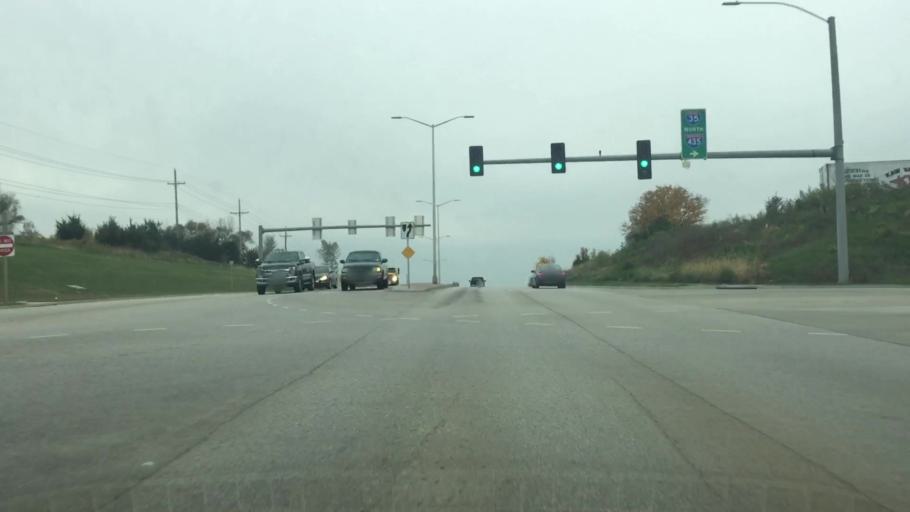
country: US
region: Kansas
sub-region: Johnson County
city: Lenexa
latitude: 38.9400
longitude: -94.7796
